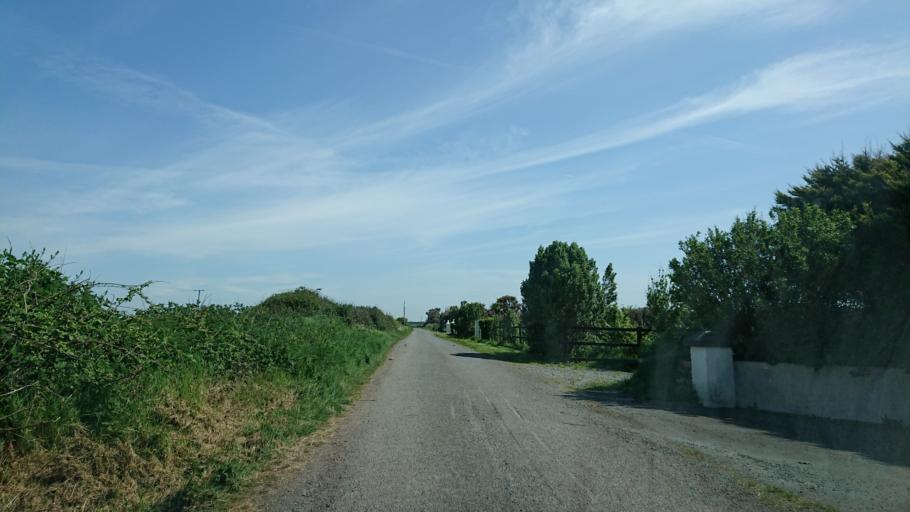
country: IE
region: Munster
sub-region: Waterford
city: Tra Mhor
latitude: 52.1366
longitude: -7.0935
